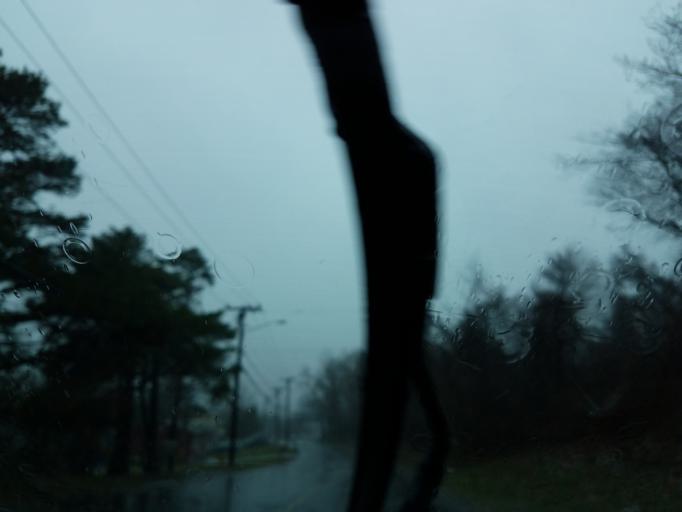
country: US
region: Connecticut
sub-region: New Haven County
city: Waterbury
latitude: 41.5284
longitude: -73.0658
